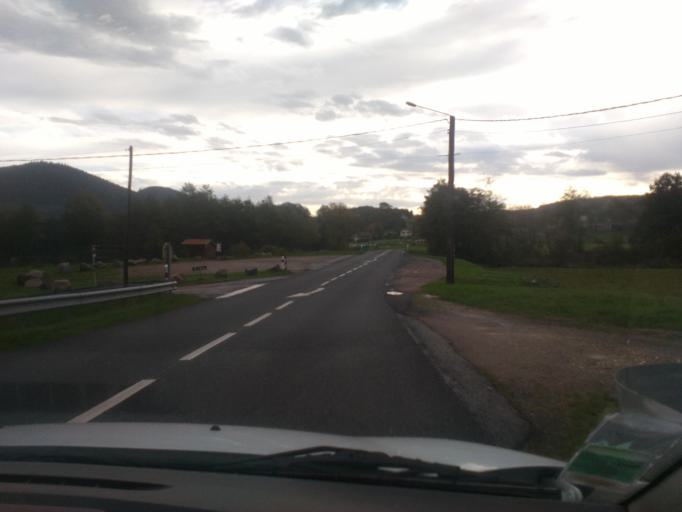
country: FR
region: Lorraine
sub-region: Departement des Vosges
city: Granges-sur-Vologne
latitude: 48.1899
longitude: 6.7802
